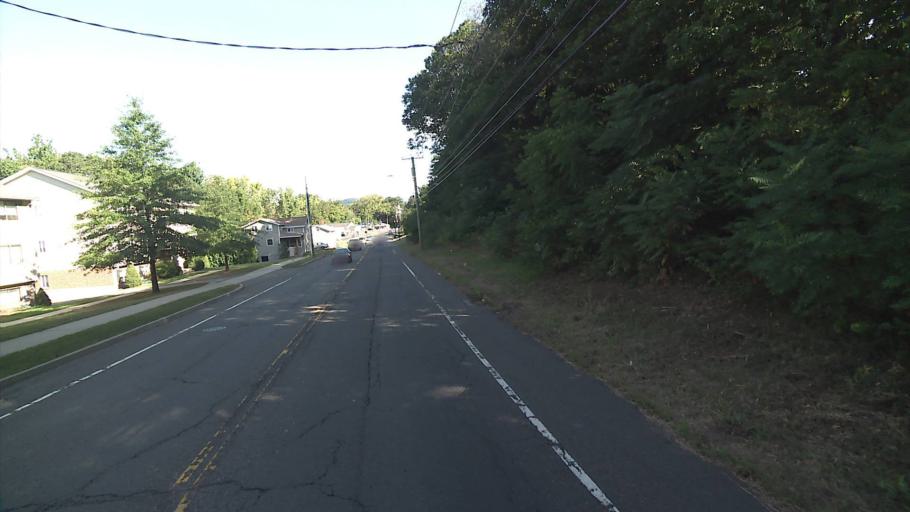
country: US
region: Connecticut
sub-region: New Haven County
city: Meriden
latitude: 41.5153
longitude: -72.8250
